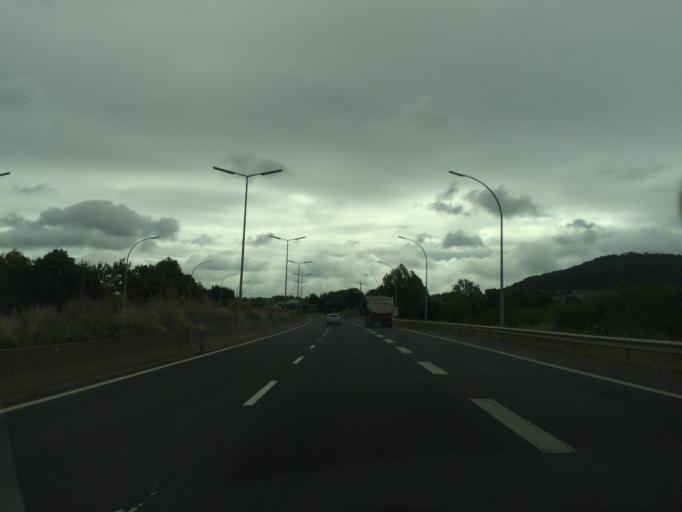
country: LU
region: Luxembourg
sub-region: Canton d'Esch-sur-Alzette
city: Kayl
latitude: 49.5009
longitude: 6.0479
